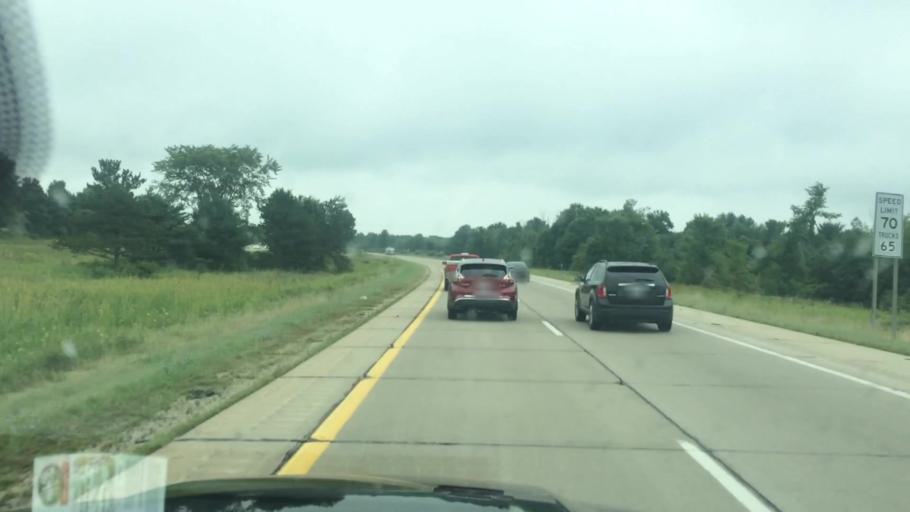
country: US
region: Michigan
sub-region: Eaton County
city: Charlotte
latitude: 42.5226
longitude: -84.8260
